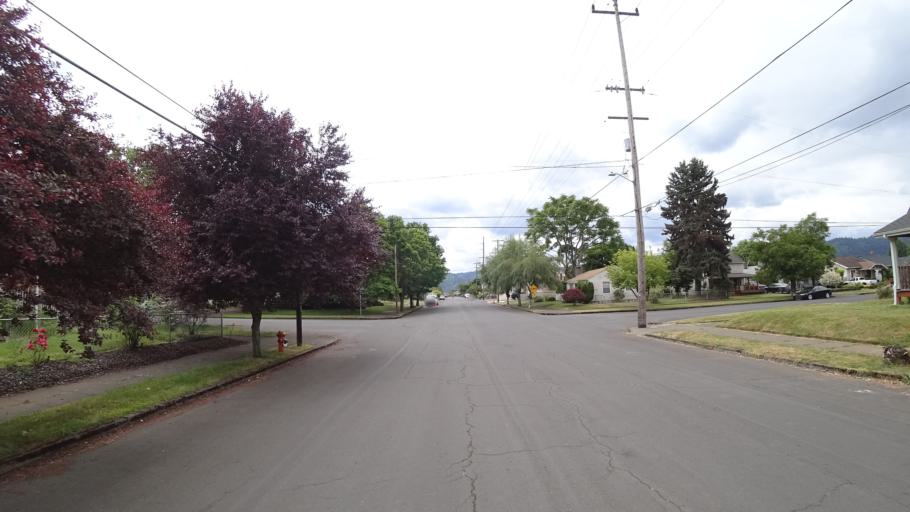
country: US
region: Oregon
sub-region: Washington County
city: West Haven
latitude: 45.5826
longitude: -122.7361
